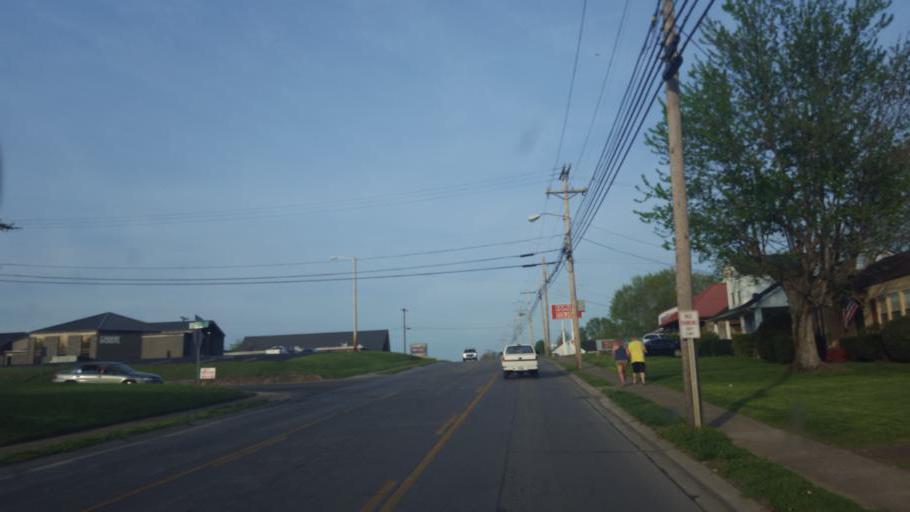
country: US
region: Kentucky
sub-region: Barren County
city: Glasgow
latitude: 36.9980
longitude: -85.9064
